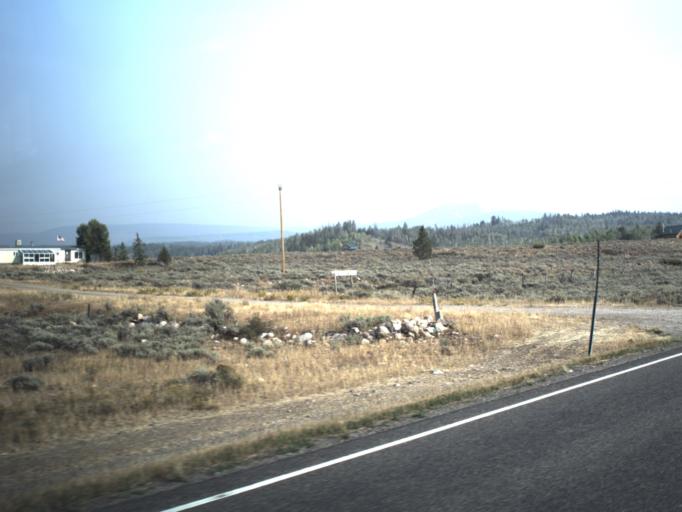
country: US
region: Wyoming
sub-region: Uinta County
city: Evanston
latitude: 40.9428
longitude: -110.8380
